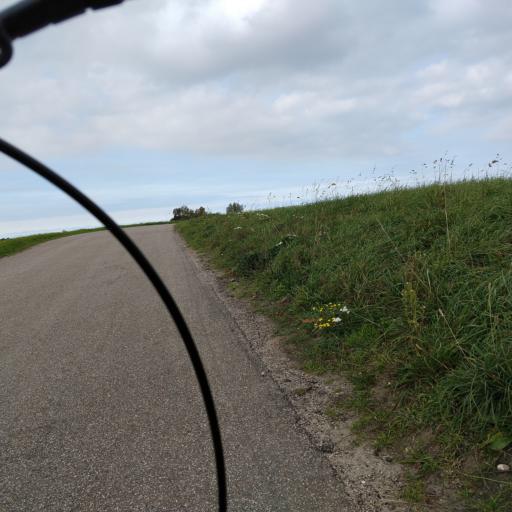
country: NL
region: South Holland
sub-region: Gemeente Goeree-Overflakkee
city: Goedereede
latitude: 51.7244
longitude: 3.9714
